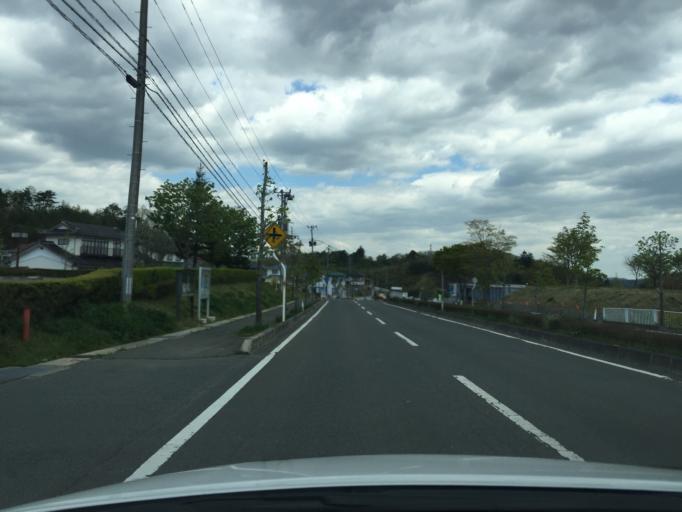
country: JP
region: Fukushima
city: Yanagawamachi-saiwaicho
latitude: 37.6788
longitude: 140.7361
